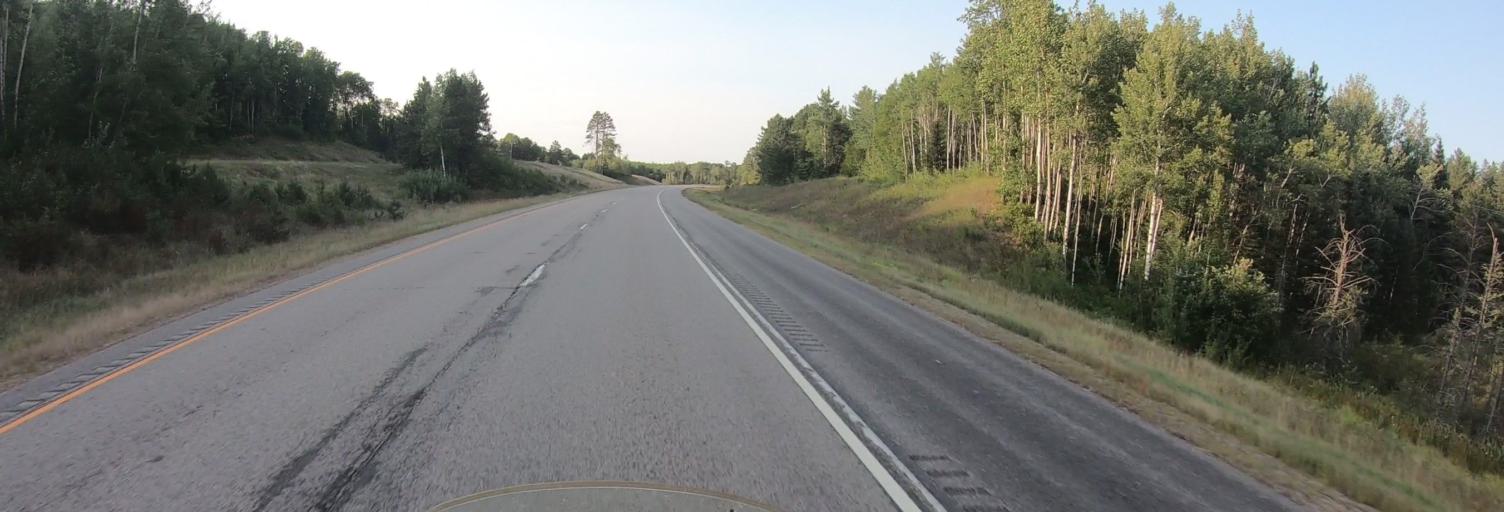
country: US
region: Minnesota
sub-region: Saint Louis County
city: Mountain Iron
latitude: 47.6833
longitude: -92.6387
